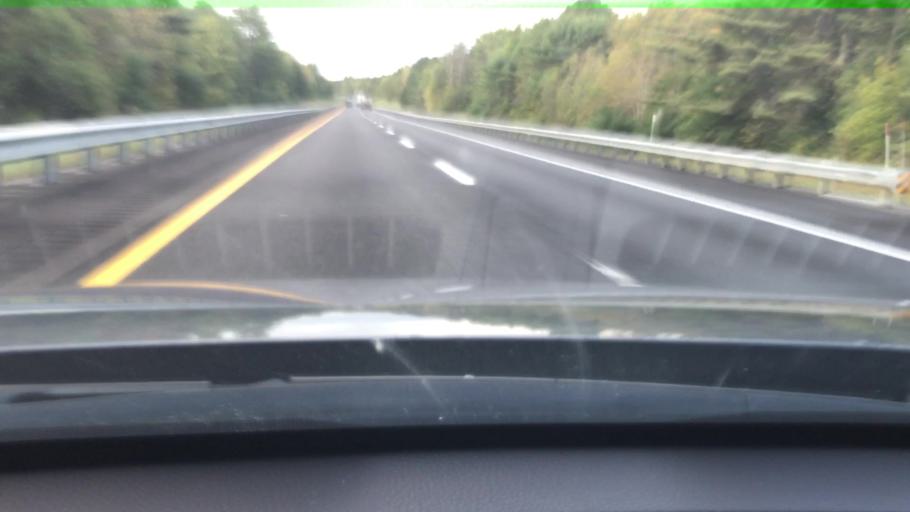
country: US
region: Maine
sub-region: Sagadahoc County
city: Richmond
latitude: 44.0606
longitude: -69.8862
